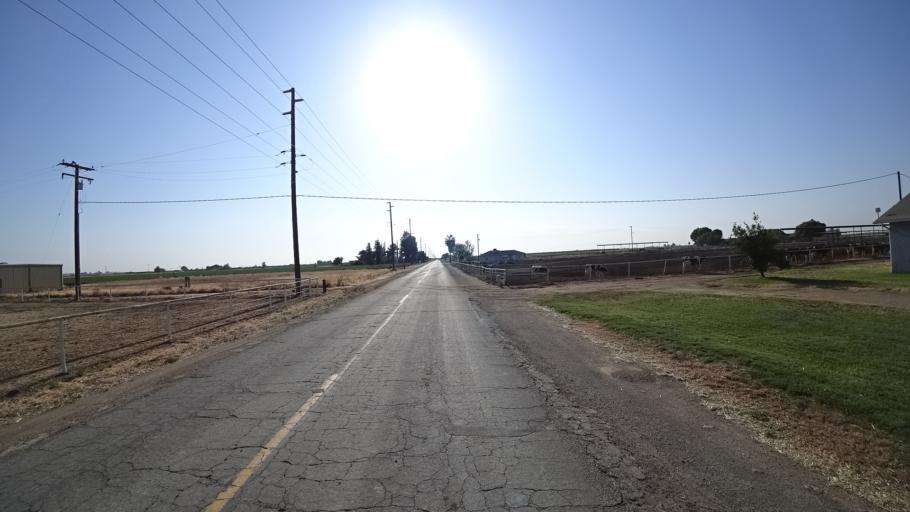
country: US
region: California
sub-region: Kings County
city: Home Garden
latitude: 36.3135
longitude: -119.5745
